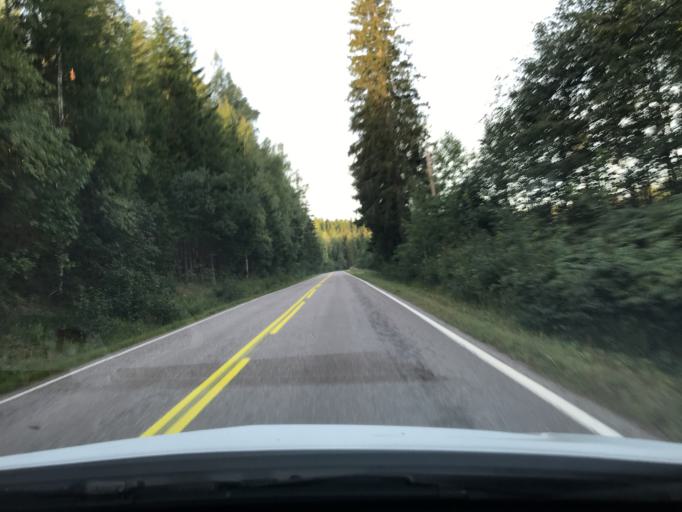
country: FI
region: Uusimaa
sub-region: Helsinki
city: Vihti
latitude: 60.4222
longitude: 24.5081
